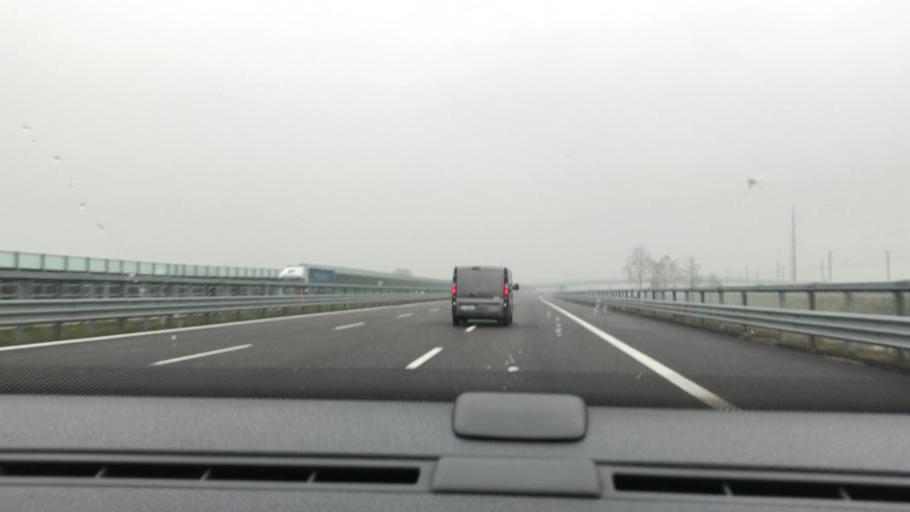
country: IT
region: Lombardy
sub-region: Provincia di Bergamo
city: Fornovo San Giovanni
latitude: 45.5106
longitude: 9.6730
